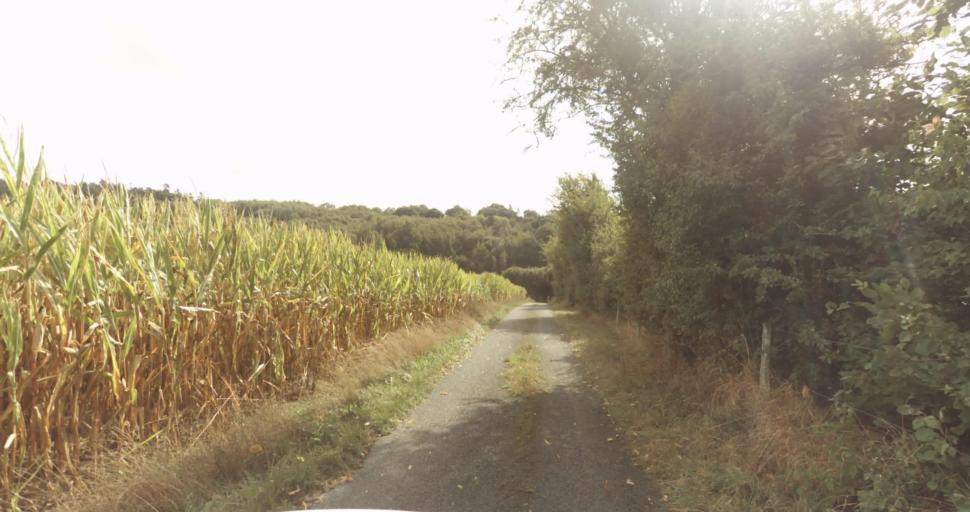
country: FR
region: Lower Normandy
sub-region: Departement de l'Orne
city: Gace
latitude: 48.8479
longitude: 0.3890
